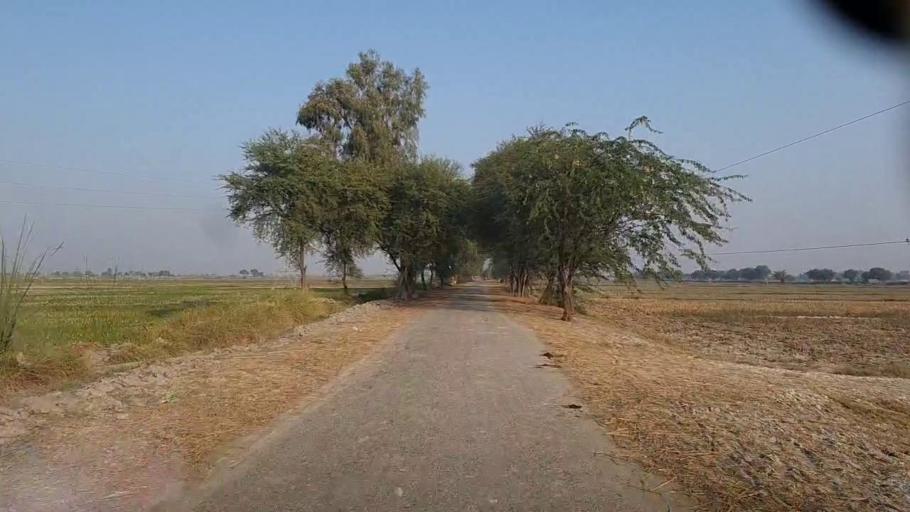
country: PK
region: Sindh
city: Jacobabad
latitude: 28.2399
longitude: 68.4908
